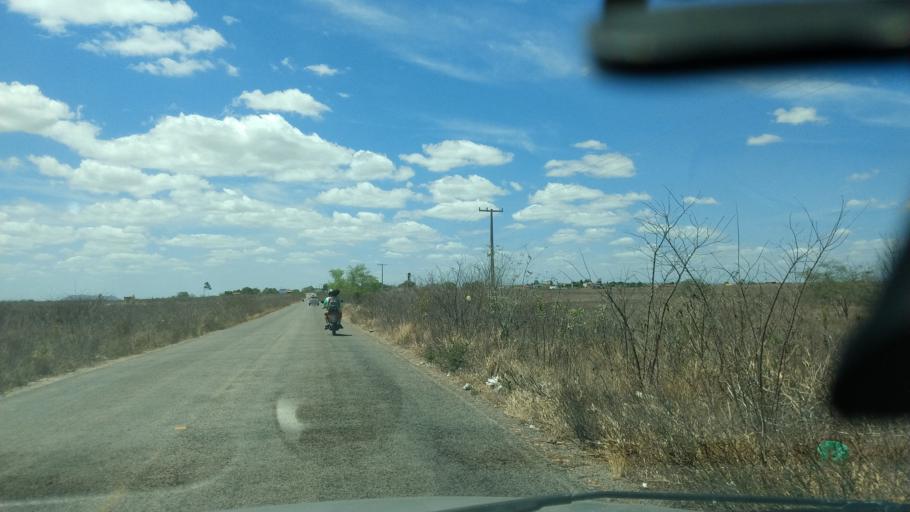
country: BR
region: Rio Grande do Norte
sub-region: Sao Paulo Do Potengi
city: Sao Paulo do Potengi
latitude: -5.9141
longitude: -35.7466
